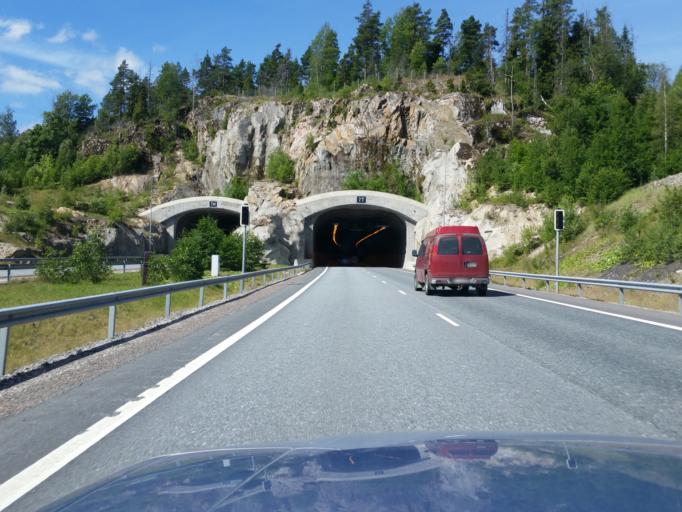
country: FI
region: Uusimaa
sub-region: Helsinki
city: Saukkola
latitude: 60.3131
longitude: 23.9958
